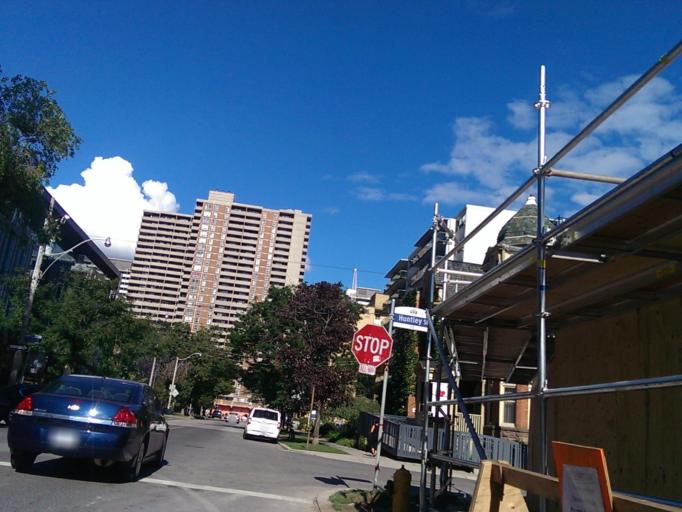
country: CA
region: Ontario
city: Toronto
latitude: 43.6690
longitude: -79.3783
